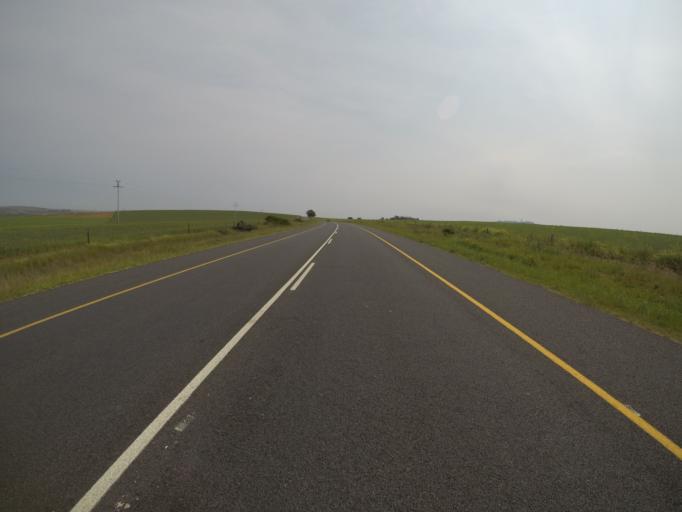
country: ZA
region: Western Cape
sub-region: West Coast District Municipality
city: Malmesbury
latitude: -33.5104
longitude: 18.8441
